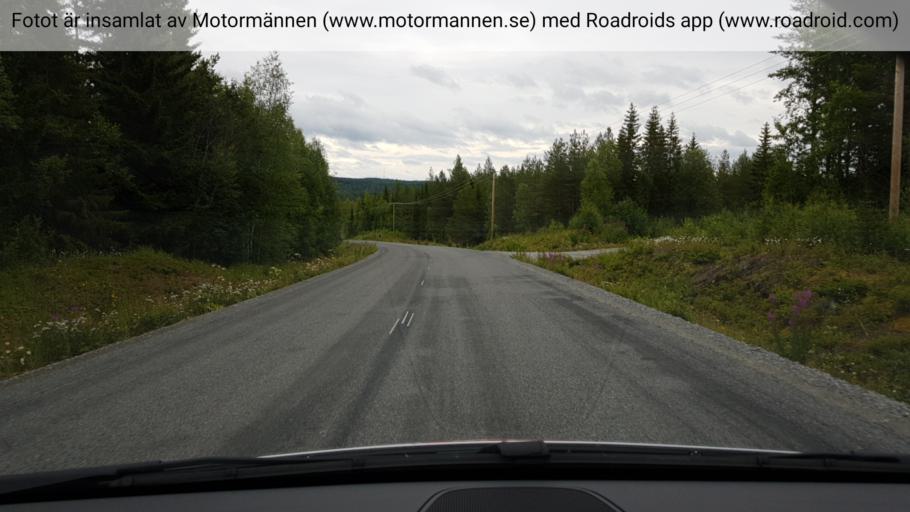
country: SE
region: Jaemtland
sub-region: Krokoms Kommun
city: Krokom
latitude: 63.6686
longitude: 14.5514
